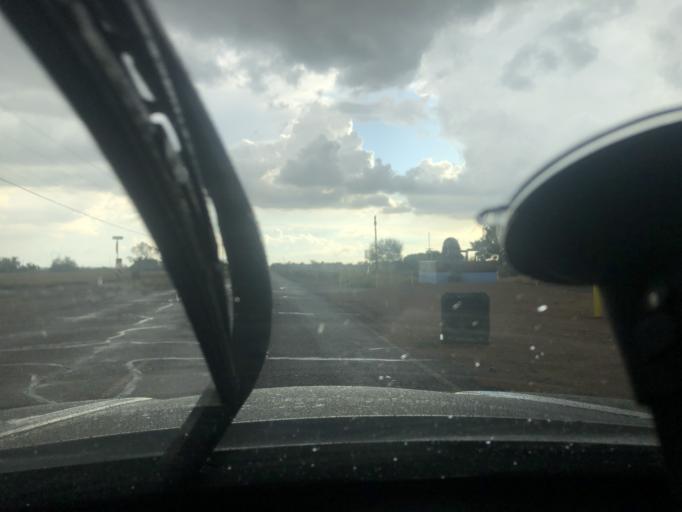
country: US
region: Arizona
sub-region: Maricopa County
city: Scottsdale
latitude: 33.4844
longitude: -111.8827
